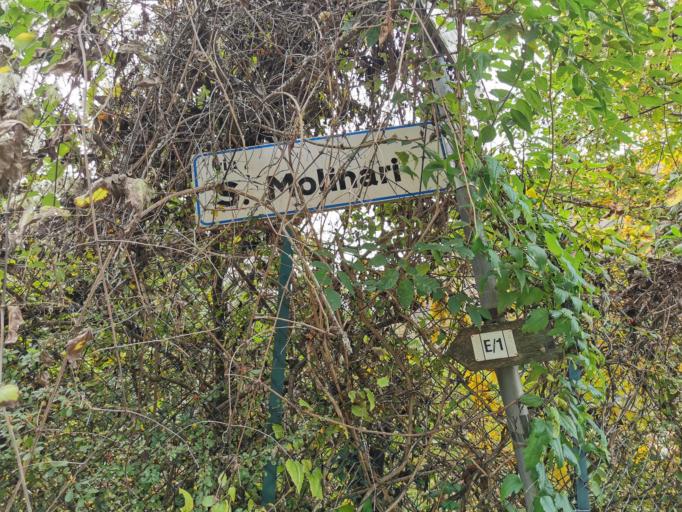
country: IT
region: Lombardy
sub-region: Provincia di Varese
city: Ganna
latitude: 45.9036
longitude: 8.8288
